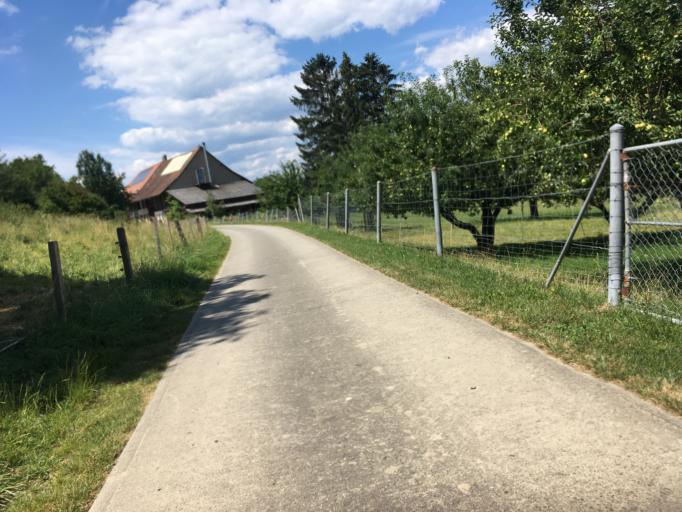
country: CH
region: Fribourg
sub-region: Broye District
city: Domdidier
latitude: 46.9283
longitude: 6.9851
